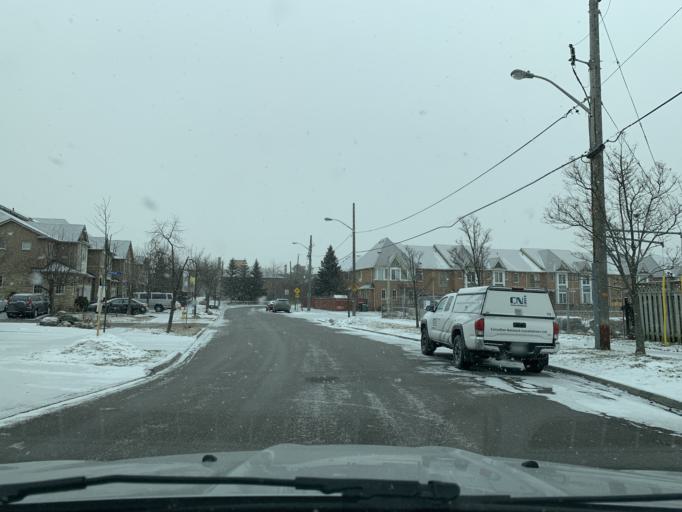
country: CA
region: Ontario
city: Concord
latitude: 43.7427
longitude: -79.4905
